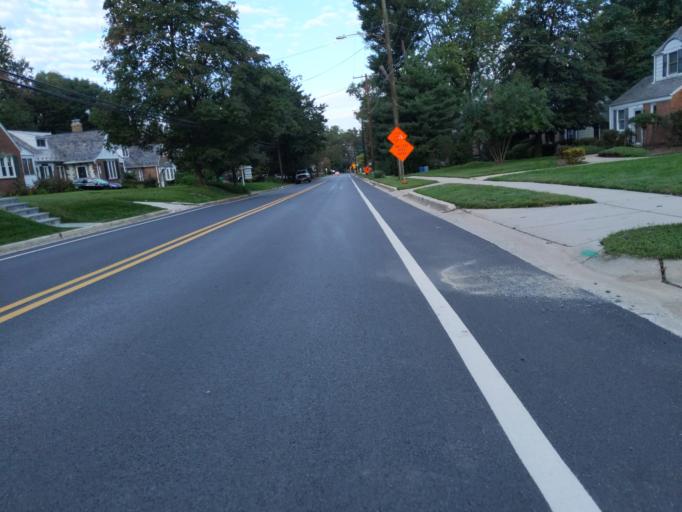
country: US
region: Maryland
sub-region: Montgomery County
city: Forest Glen
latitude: 39.0100
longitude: -77.0454
